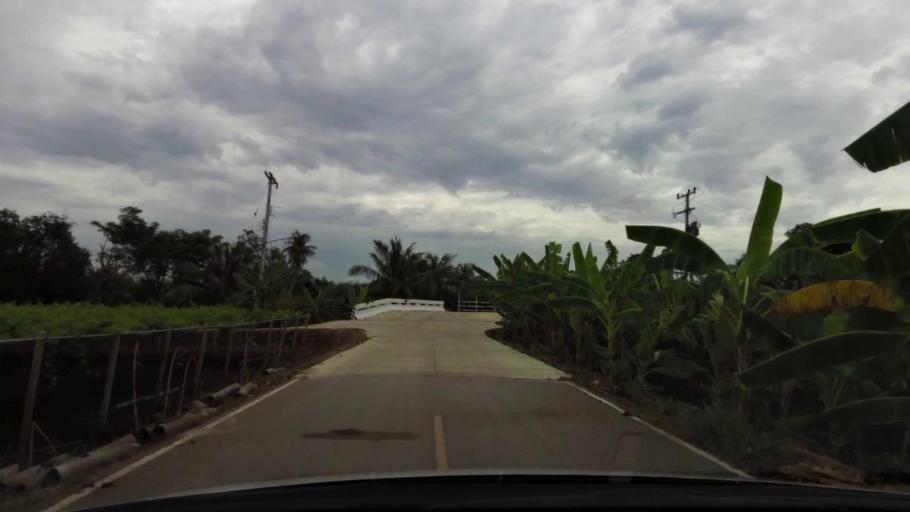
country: TH
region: Ratchaburi
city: Damnoen Saduak
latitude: 13.5521
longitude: 99.9760
